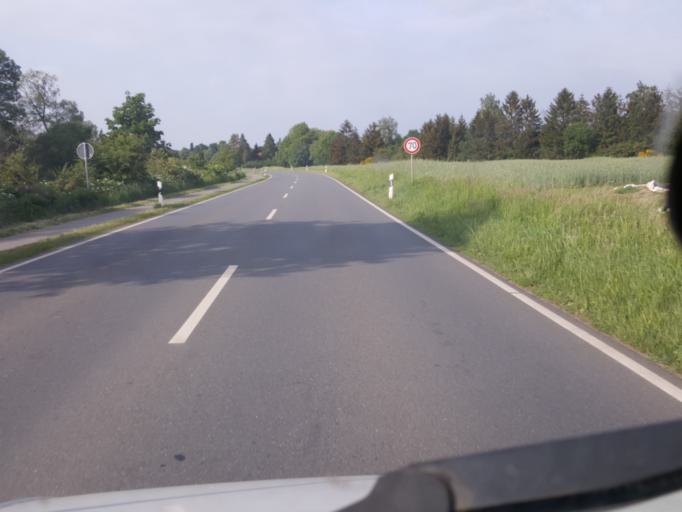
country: DE
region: Lower Saxony
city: Liebenau
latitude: 52.5945
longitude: 9.0971
